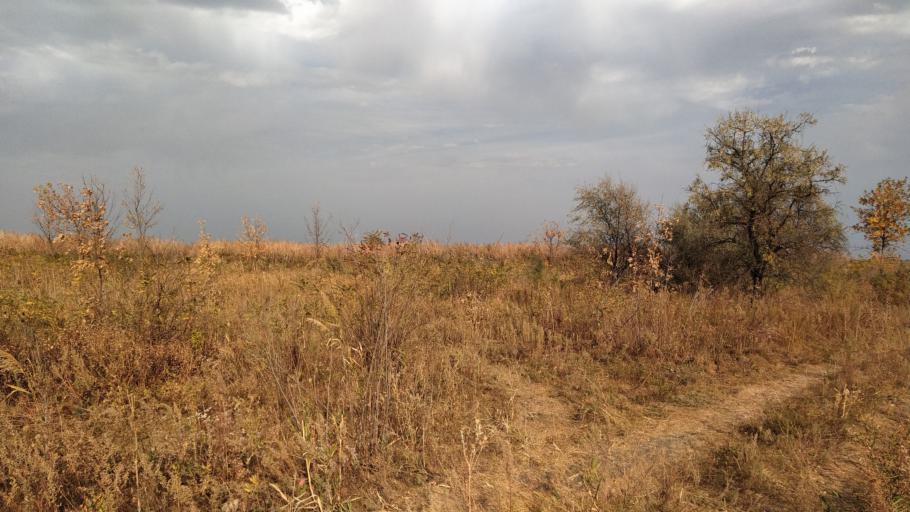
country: RU
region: Rostov
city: Kuleshovka
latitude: 47.1421
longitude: 39.5860
